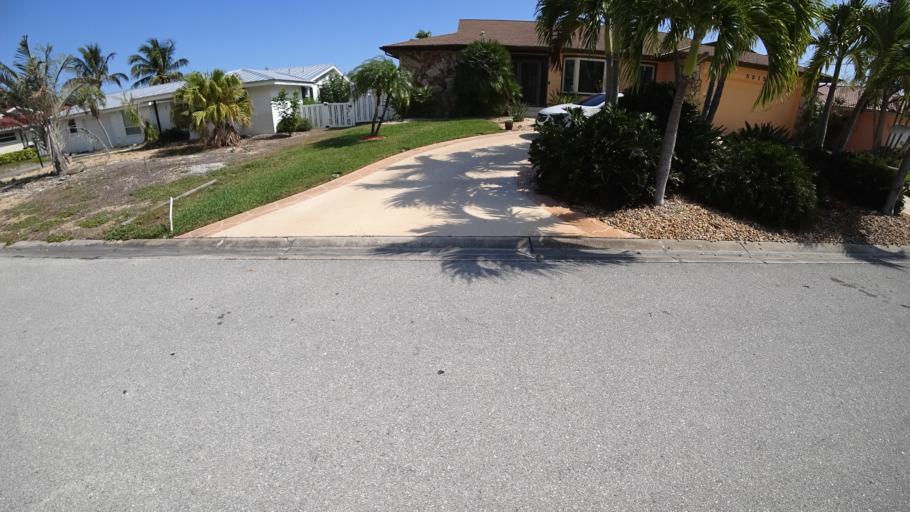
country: US
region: Florida
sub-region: Manatee County
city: Cortez
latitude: 27.4528
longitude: -82.6537
